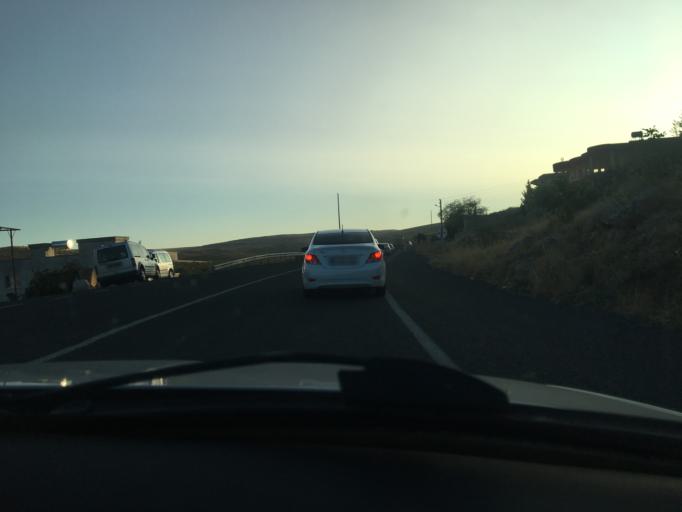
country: TR
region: Sanliurfa
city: Halfeti
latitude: 37.2038
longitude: 37.9706
